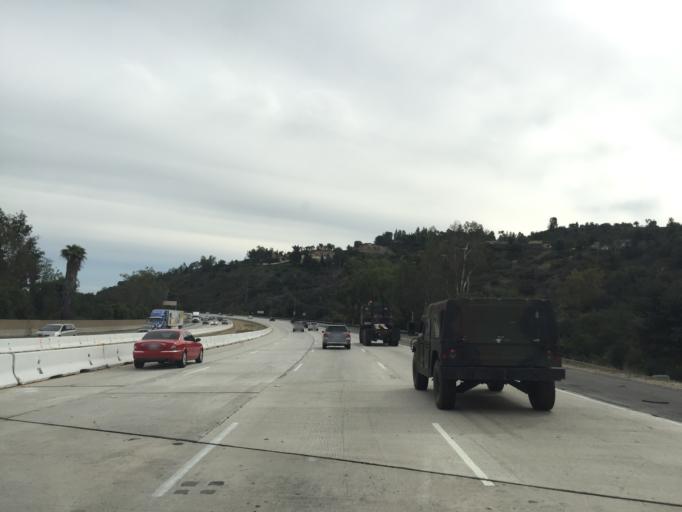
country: US
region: California
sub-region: Los Angeles County
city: La Canada Flintridge
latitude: 34.1901
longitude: -118.1811
